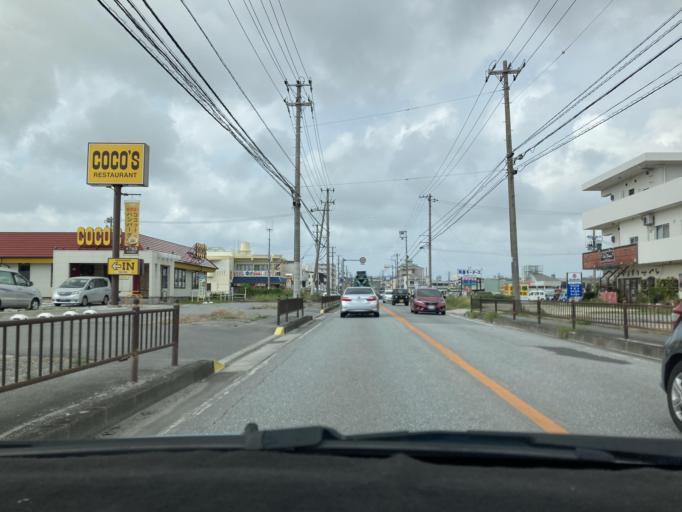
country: JP
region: Okinawa
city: Tomigusuku
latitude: 26.1674
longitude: 127.6679
